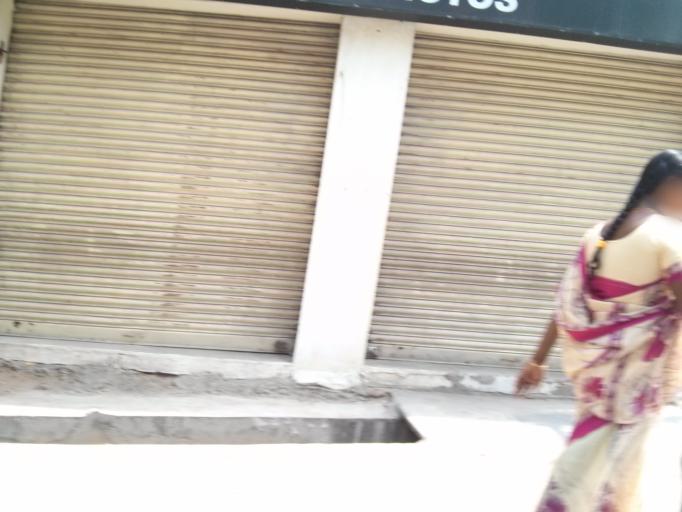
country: IN
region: Tamil Nadu
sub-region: Coimbatore
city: Coimbatore
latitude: 11.0143
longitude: 76.9653
